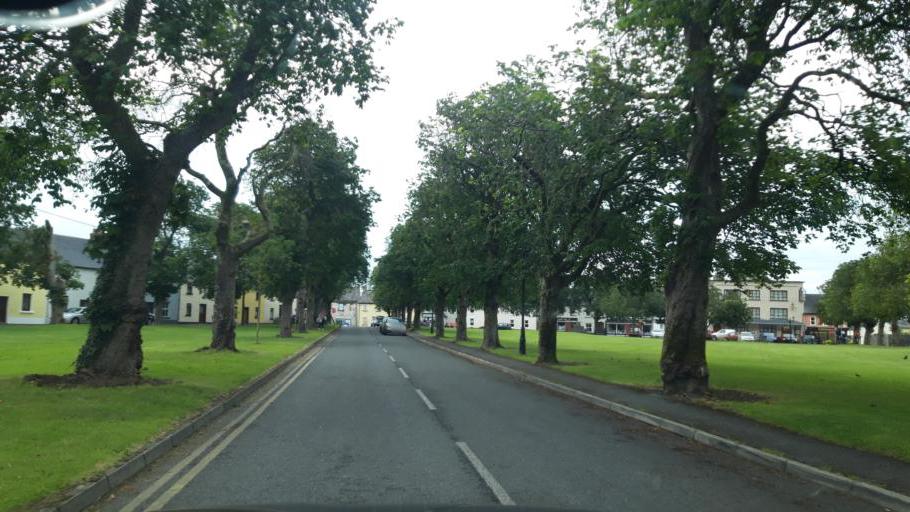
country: IE
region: Leinster
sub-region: Kilkenny
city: Ballyragget
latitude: 52.7314
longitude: -7.3986
